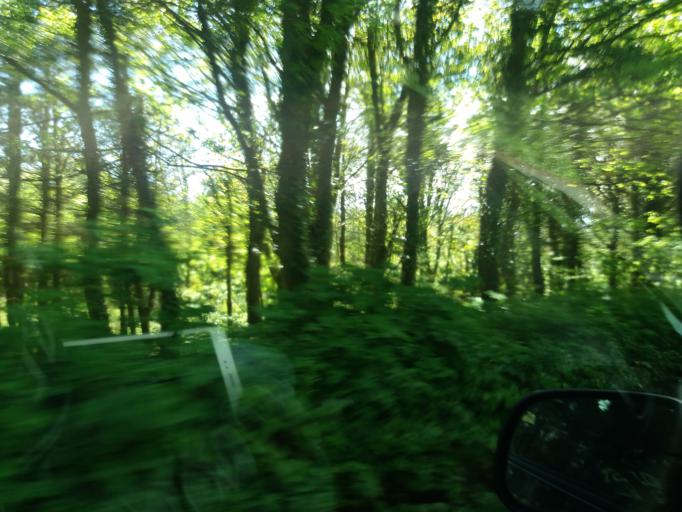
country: IE
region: Munster
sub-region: Waterford
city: Dunmore East
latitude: 52.2420
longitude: -6.9436
